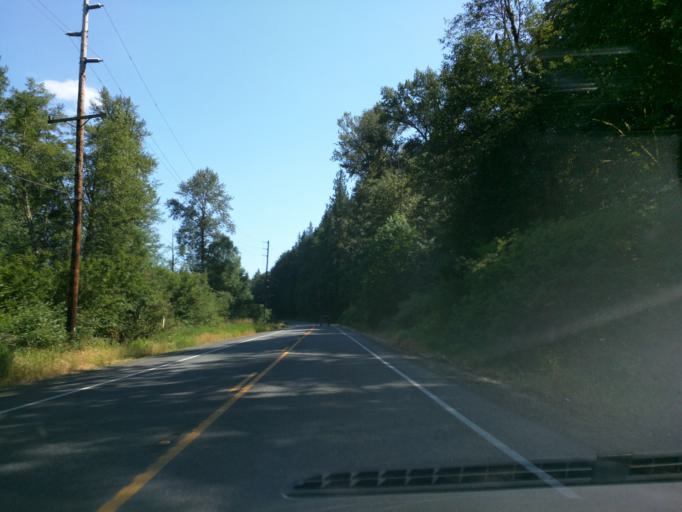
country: US
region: Washington
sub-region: Whatcom County
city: Peaceful Valley
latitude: 48.8758
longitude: -122.1571
